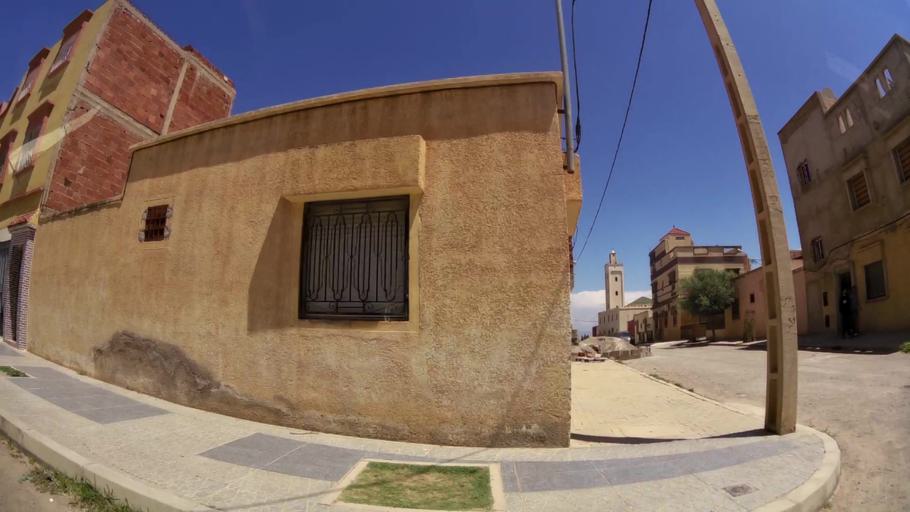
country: MA
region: Oriental
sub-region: Oujda-Angad
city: Oujda
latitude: 34.6908
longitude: -1.9518
